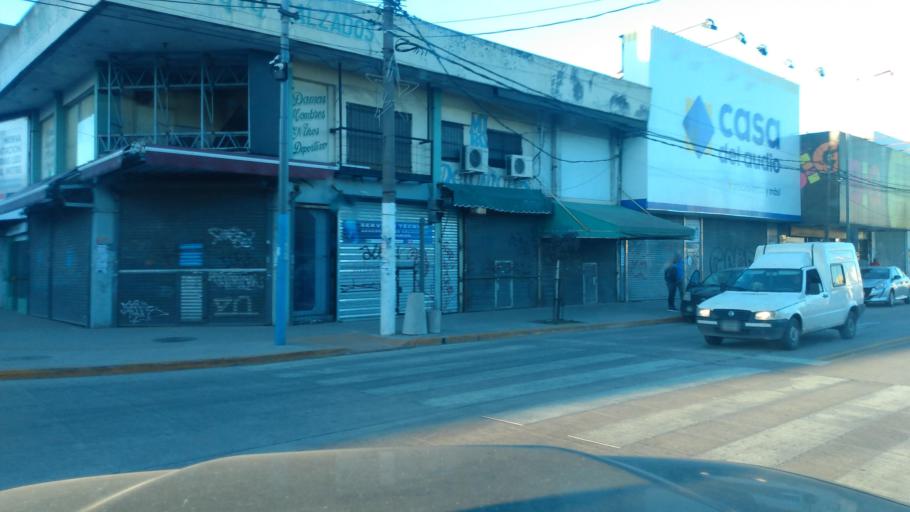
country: AR
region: Buenos Aires
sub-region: Partido de Merlo
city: Merlo
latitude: -34.6491
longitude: -58.7899
